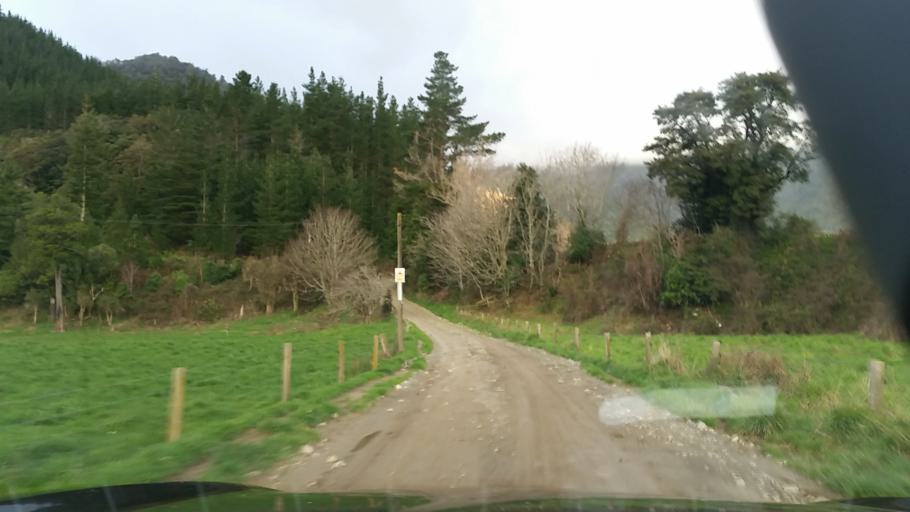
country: NZ
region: Marlborough
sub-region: Marlborough District
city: Picton
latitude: -41.2049
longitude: 173.6879
